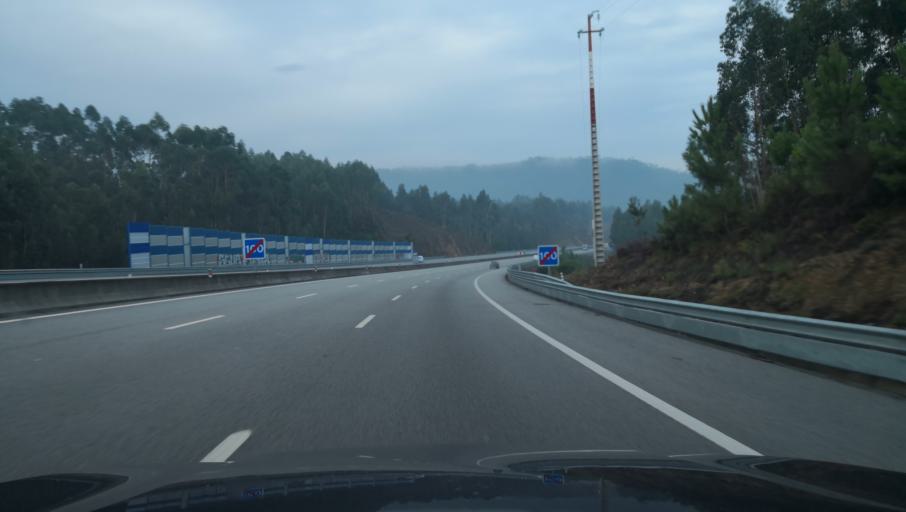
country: PT
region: Porto
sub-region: Paredes
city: Recarei
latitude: 41.1082
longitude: -8.4345
